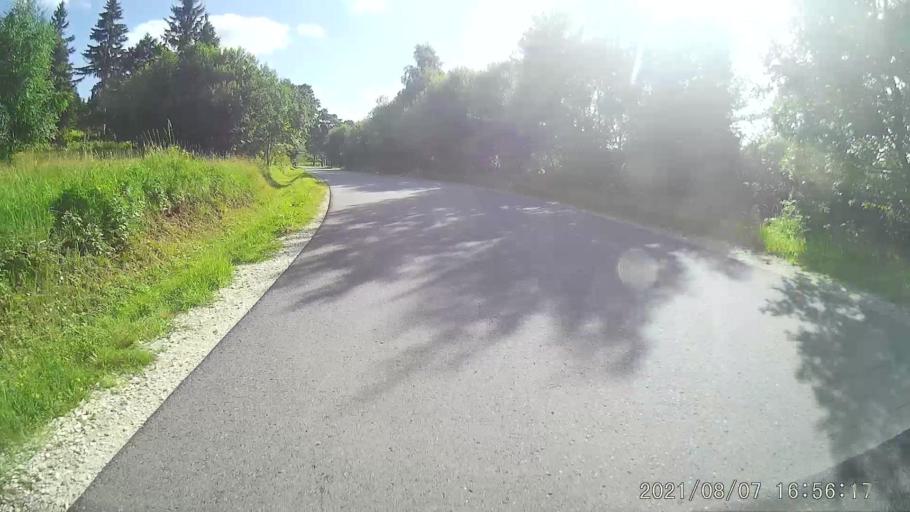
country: PL
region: Lower Silesian Voivodeship
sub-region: Powiat klodzki
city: Bystrzyca Klodzka
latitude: 50.2809
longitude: 16.5411
